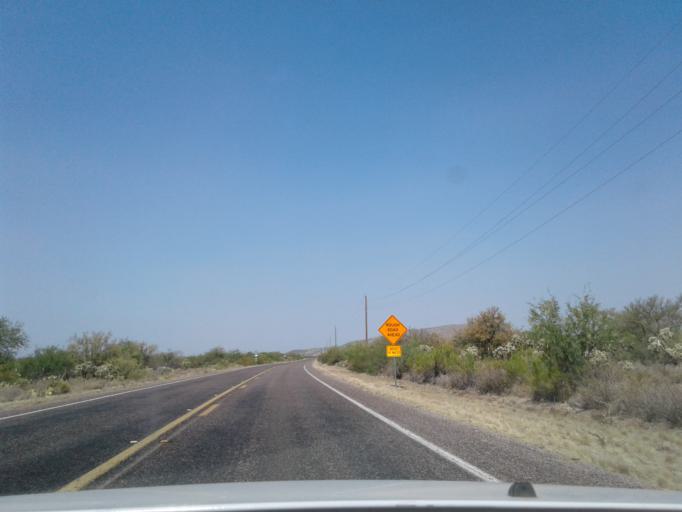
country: US
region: Arizona
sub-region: Pima County
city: Catalina
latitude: 32.6577
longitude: -111.0850
